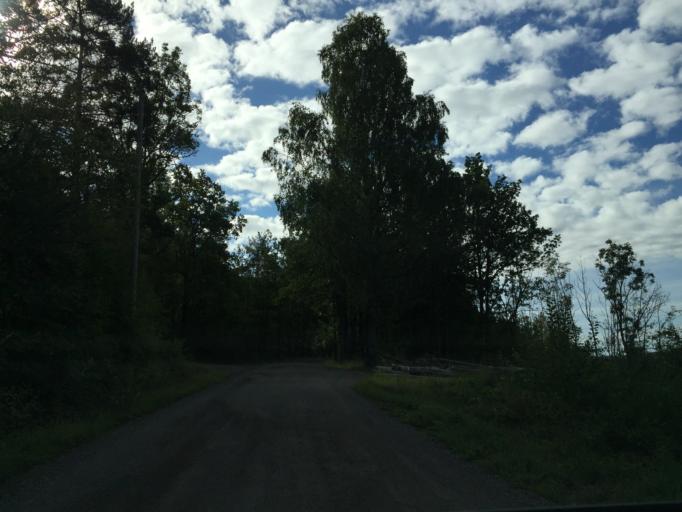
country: NO
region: Vestfold
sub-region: Holmestrand
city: Gullhaug
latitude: 59.4721
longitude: 10.1931
